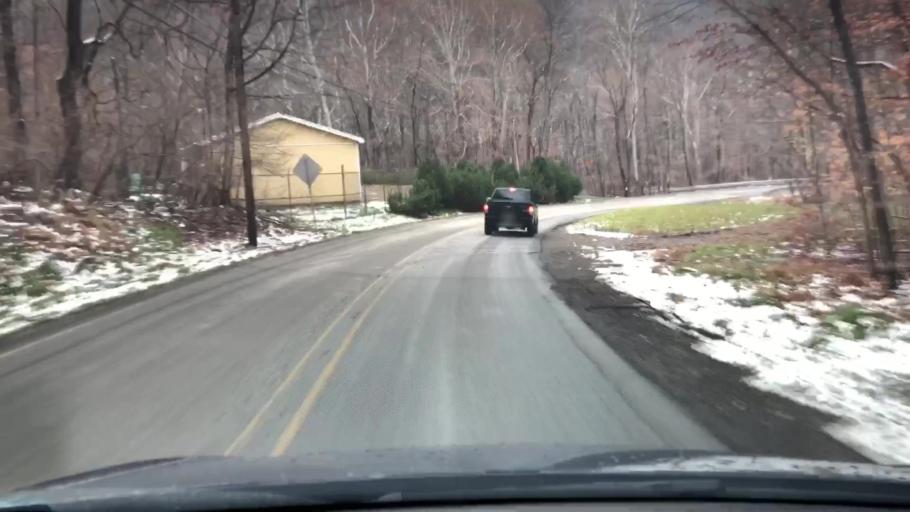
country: US
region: Pennsylvania
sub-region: Fayette County
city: Dunbar
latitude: 39.9439
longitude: -79.5785
